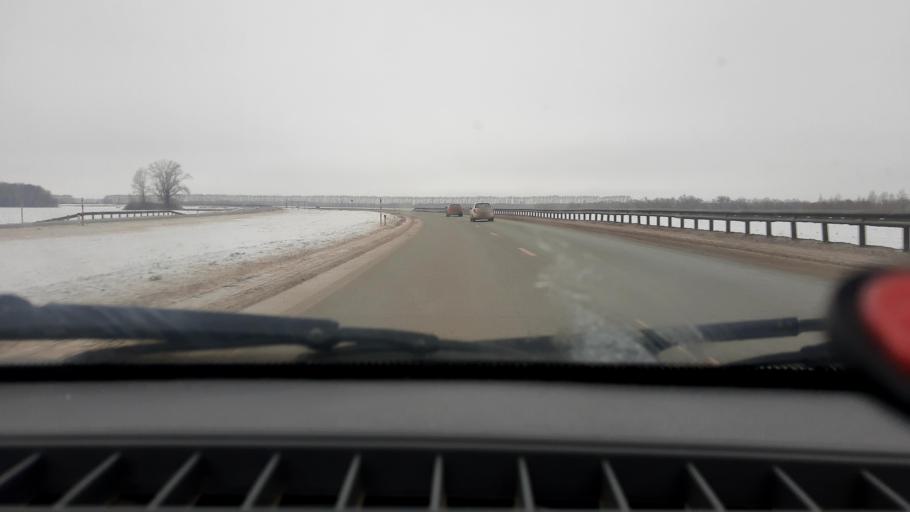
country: RU
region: Bashkortostan
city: Asanovo
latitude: 54.9784
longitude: 55.5675
